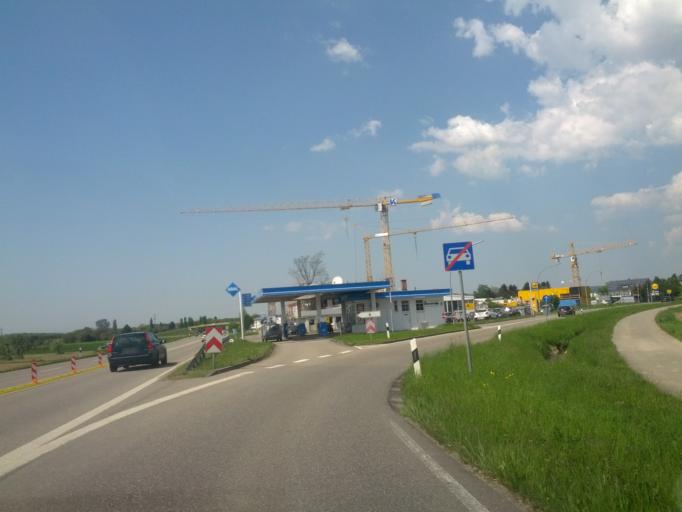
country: DE
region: Baden-Wuerttemberg
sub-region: Freiburg Region
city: Denzlingen
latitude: 48.0649
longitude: 7.8689
